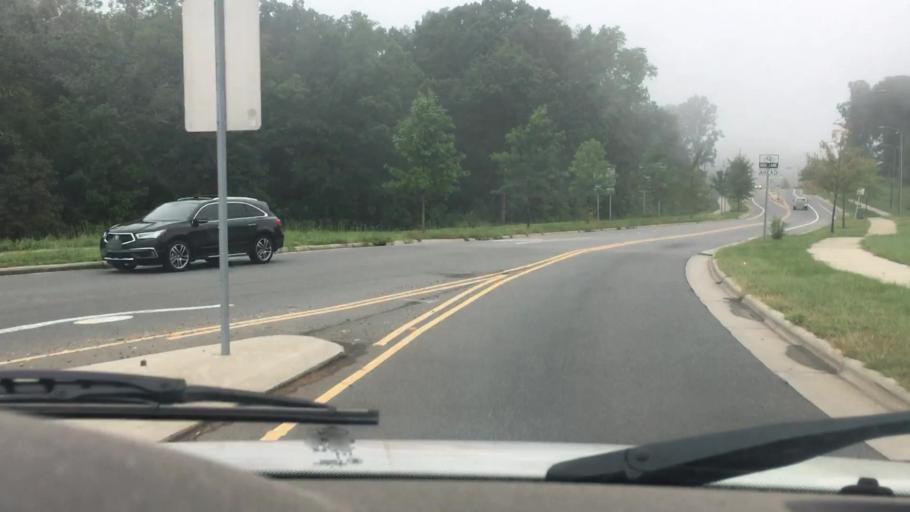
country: US
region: North Carolina
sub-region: Mecklenburg County
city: Huntersville
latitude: 35.3700
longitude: -80.7893
